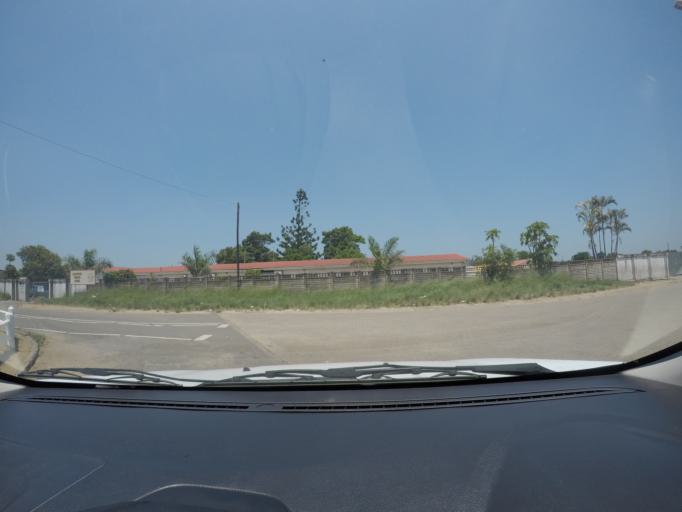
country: ZA
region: KwaZulu-Natal
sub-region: uThungulu District Municipality
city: eSikhawini
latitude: -28.8859
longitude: 31.8903
